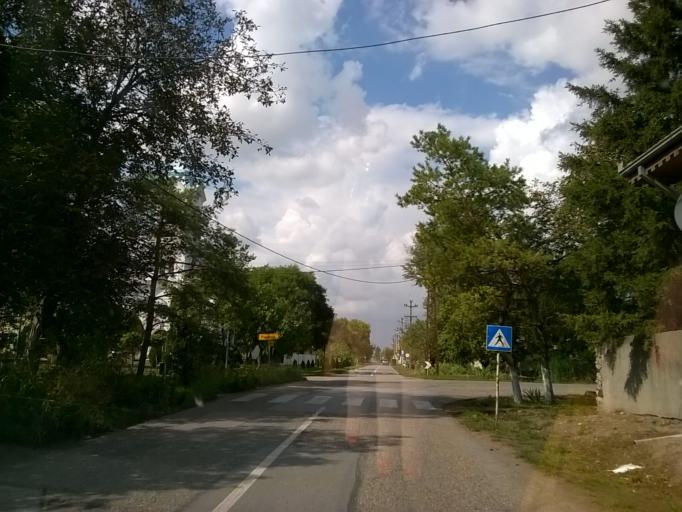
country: RS
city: Janosik
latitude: 45.1703
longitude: 21.0085
